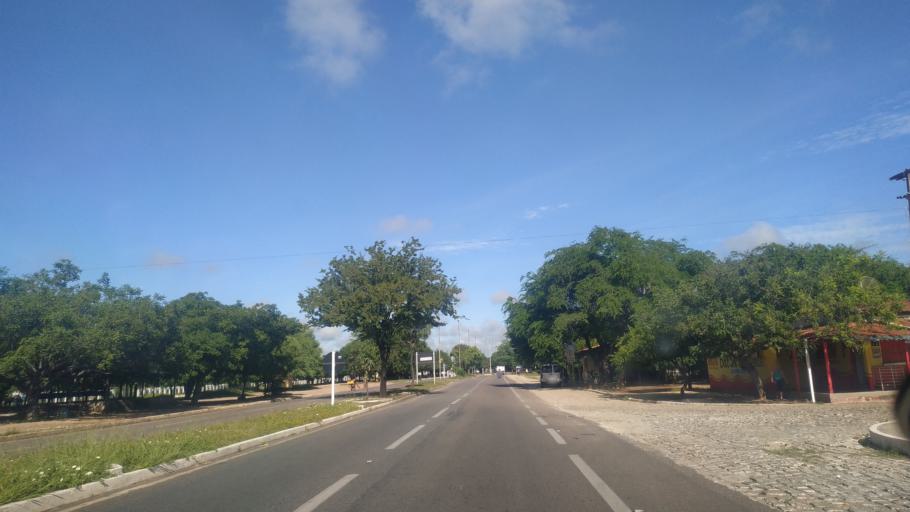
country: BR
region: Rio Grande do Norte
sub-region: Mossoro
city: Mossoro
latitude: -5.1915
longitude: -37.3608
